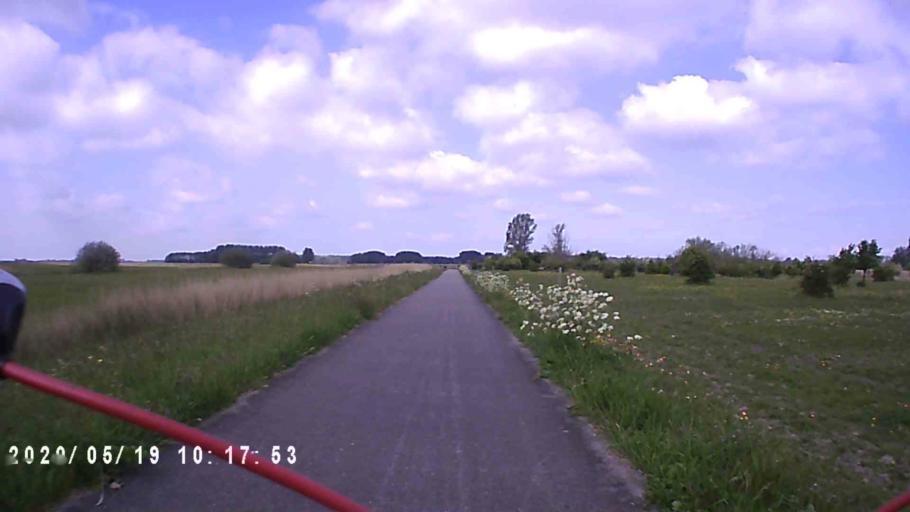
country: NL
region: Friesland
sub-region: Gemeente Kollumerland en Nieuwkruisland
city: Kollum
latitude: 53.3225
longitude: 6.2066
